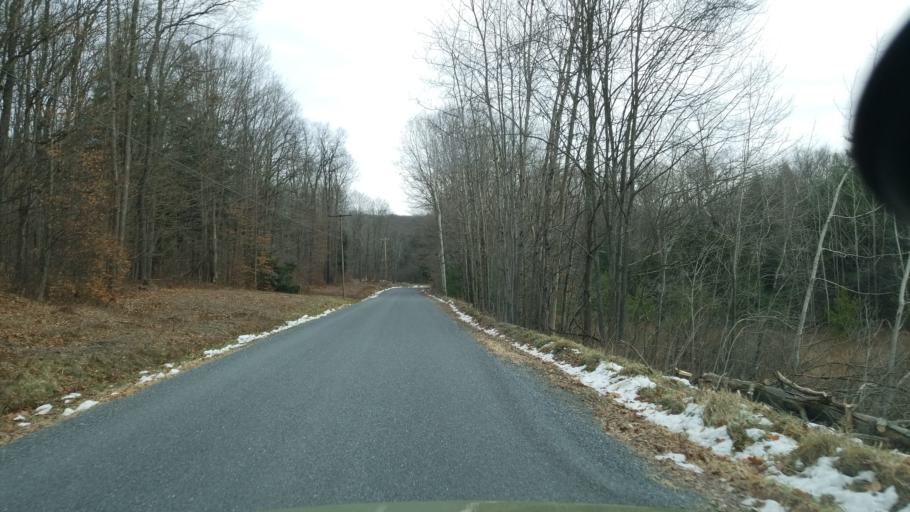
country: US
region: Pennsylvania
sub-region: Clearfield County
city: Treasure Lake
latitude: 41.1460
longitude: -78.5820
